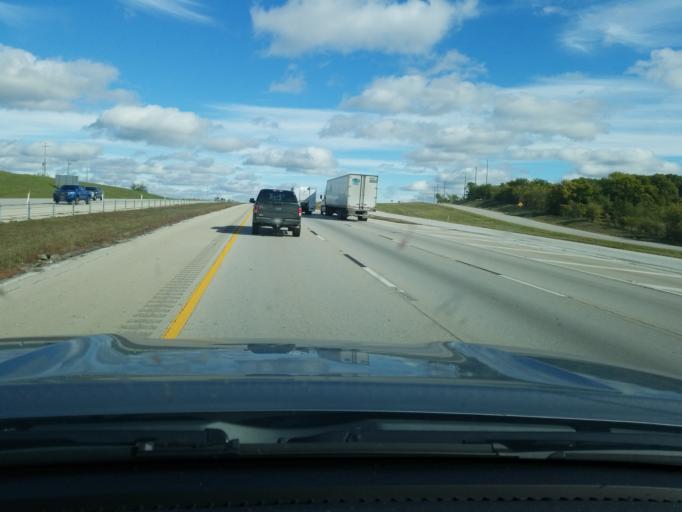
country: US
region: Texas
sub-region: Parker County
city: Aledo
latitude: 32.7294
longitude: -97.6069
